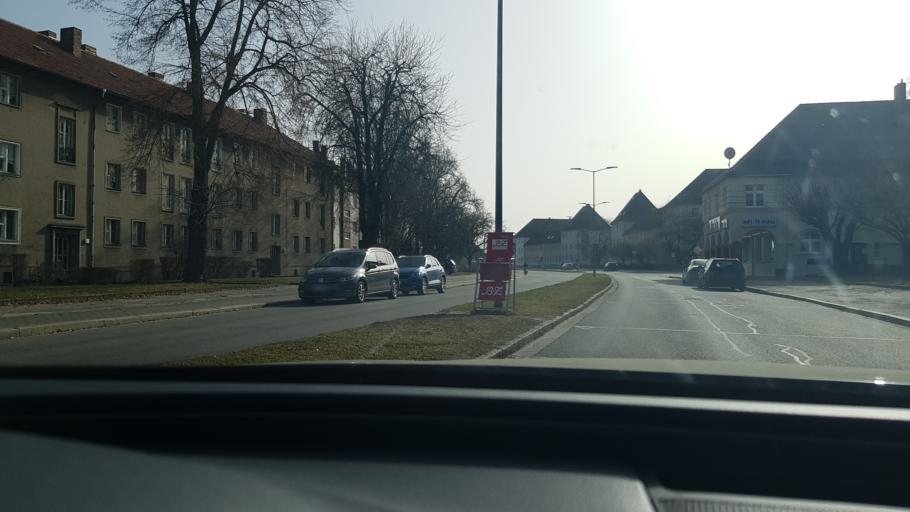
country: DE
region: Brandenburg
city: Guben
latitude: 51.9442
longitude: 14.7044
